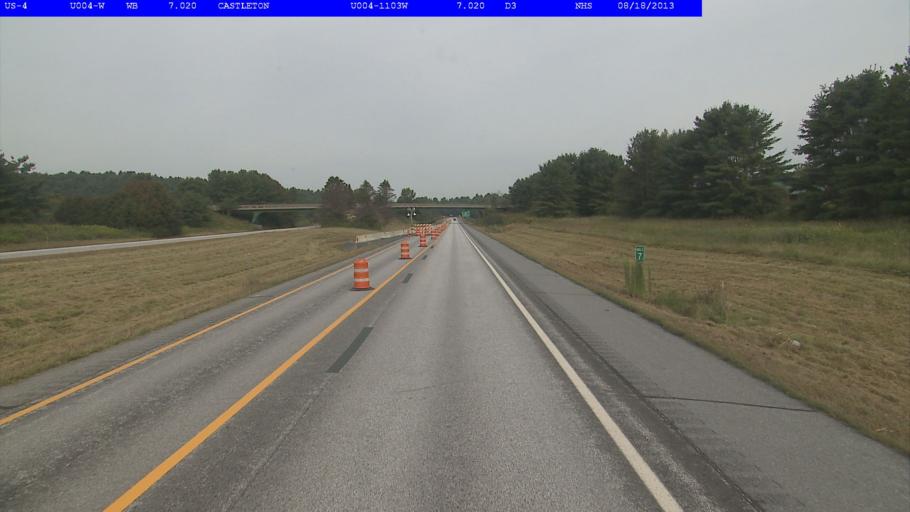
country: US
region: Vermont
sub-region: Rutland County
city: Castleton
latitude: 43.6185
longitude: -73.1795
